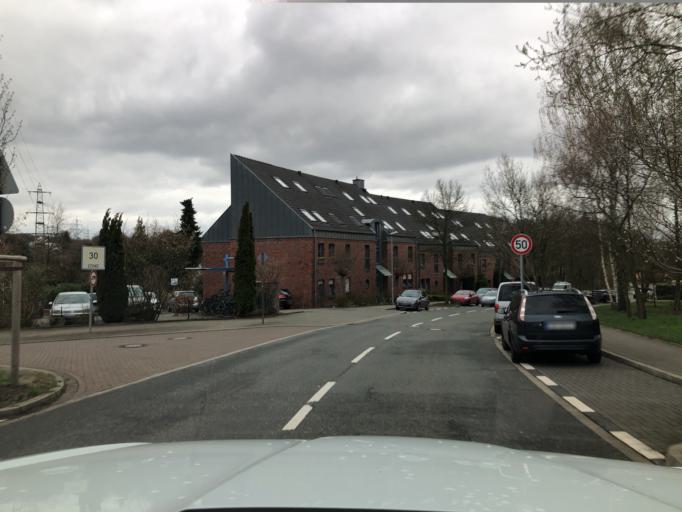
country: DE
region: North Rhine-Westphalia
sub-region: Regierungsbezirk Dusseldorf
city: Muelheim (Ruhr)
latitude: 51.4014
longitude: 6.8615
